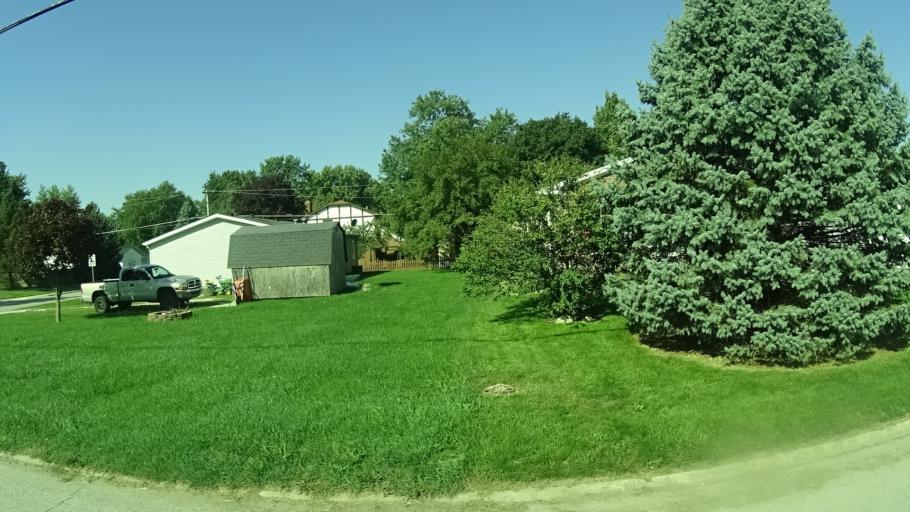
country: US
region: Indiana
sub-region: Madison County
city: Lapel
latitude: 40.0728
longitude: -85.8440
